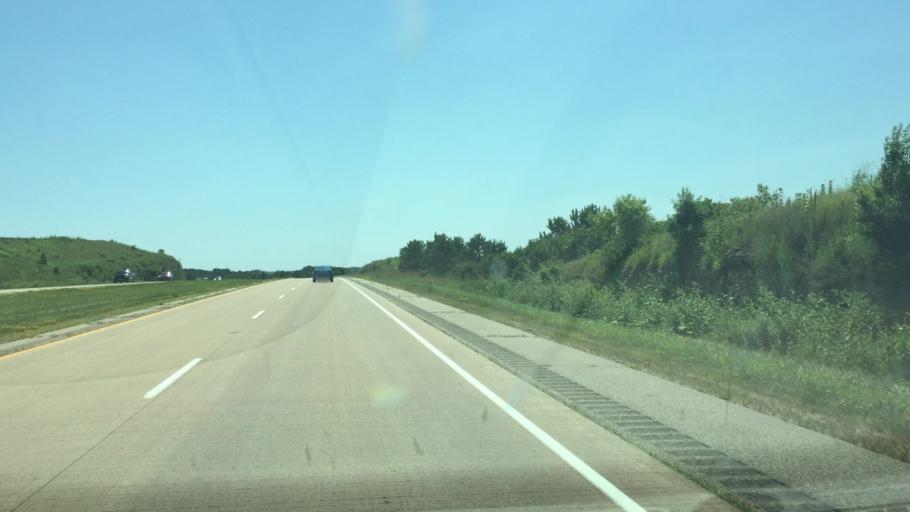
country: US
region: Wisconsin
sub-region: Iowa County
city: Mineral Point
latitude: 42.8657
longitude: -90.1980
